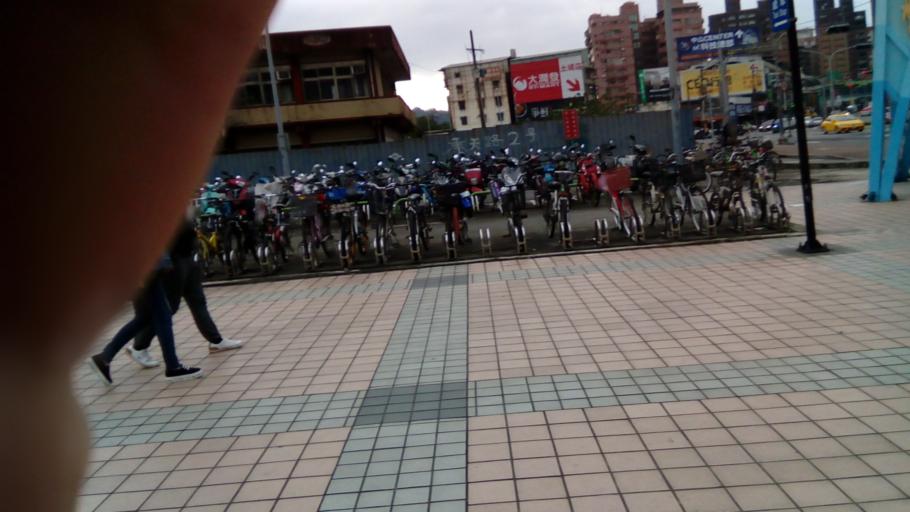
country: TW
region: Taipei
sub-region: Taipei
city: Banqiao
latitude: 24.9660
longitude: 121.4357
